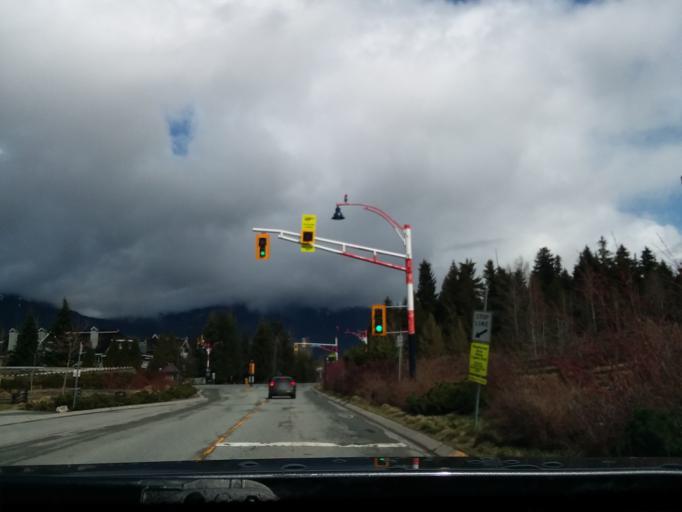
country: CA
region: British Columbia
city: Whistler
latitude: 50.1197
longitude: -122.9541
